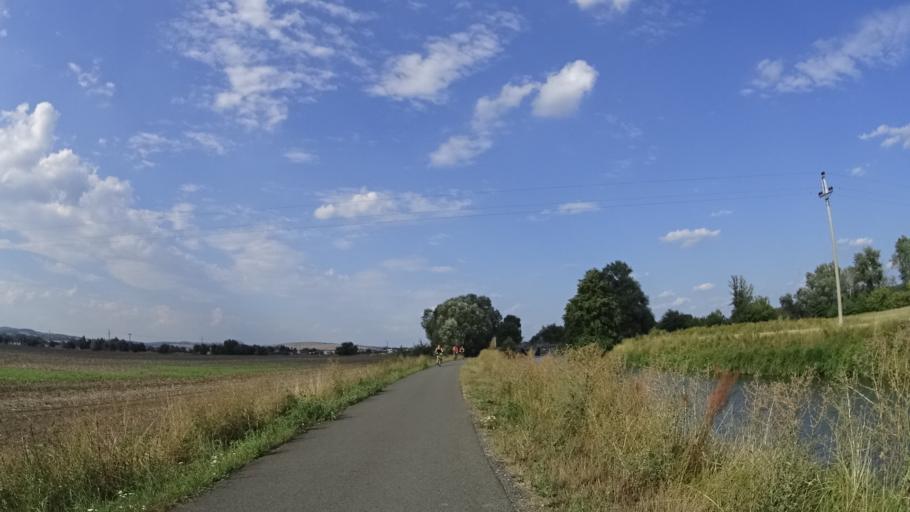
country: CZ
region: Zlin
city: Babice
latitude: 49.1101
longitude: 17.4787
